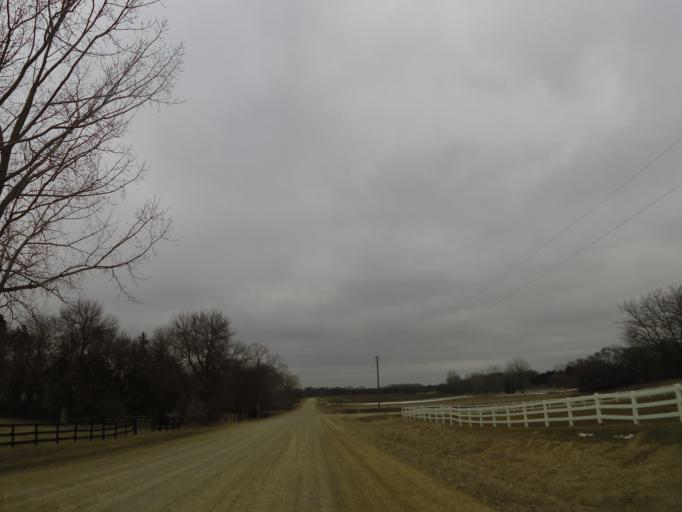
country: US
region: Minnesota
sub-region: Scott County
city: Prior Lake
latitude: 44.6853
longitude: -93.4306
